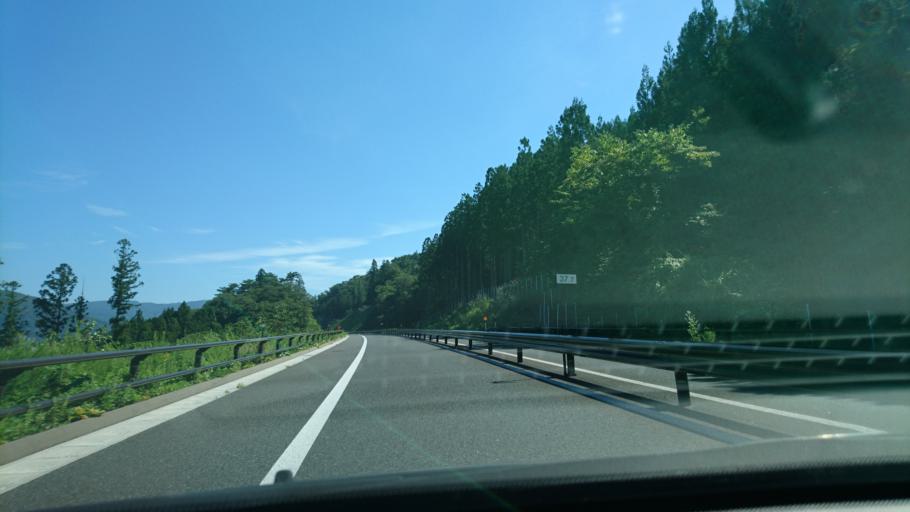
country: JP
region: Iwate
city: Tono
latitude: 39.3038
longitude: 141.4356
